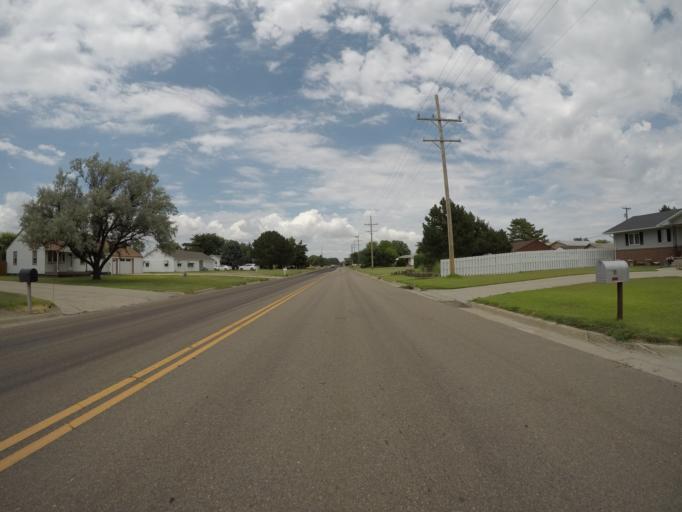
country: US
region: Kansas
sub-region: Rawlins County
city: Atwood
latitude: 39.8008
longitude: -101.0469
